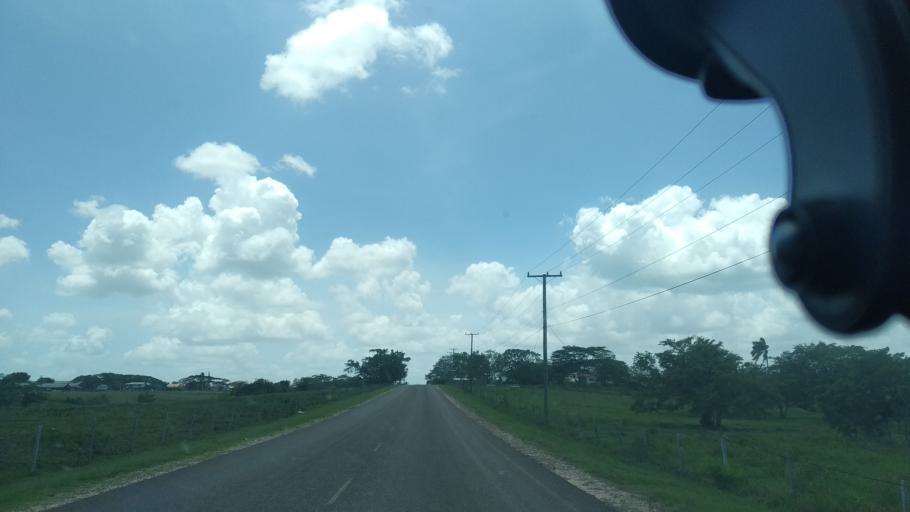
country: BZ
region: Cayo
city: San Ignacio
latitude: 17.2502
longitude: -88.9874
